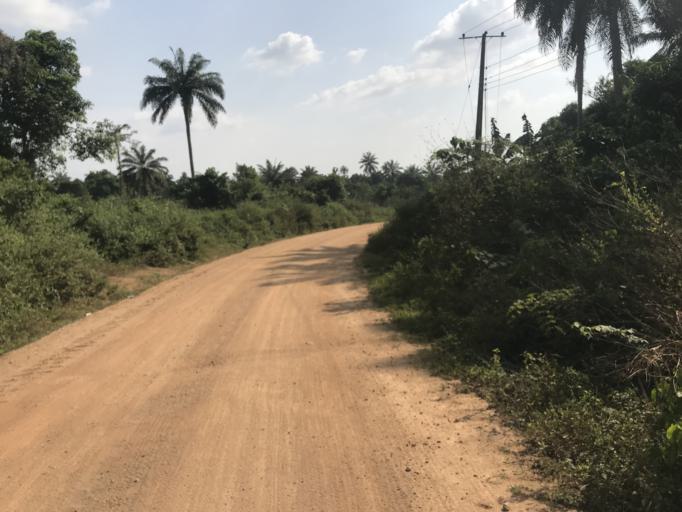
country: NG
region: Osun
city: Osogbo
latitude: 7.8603
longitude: 4.5885
